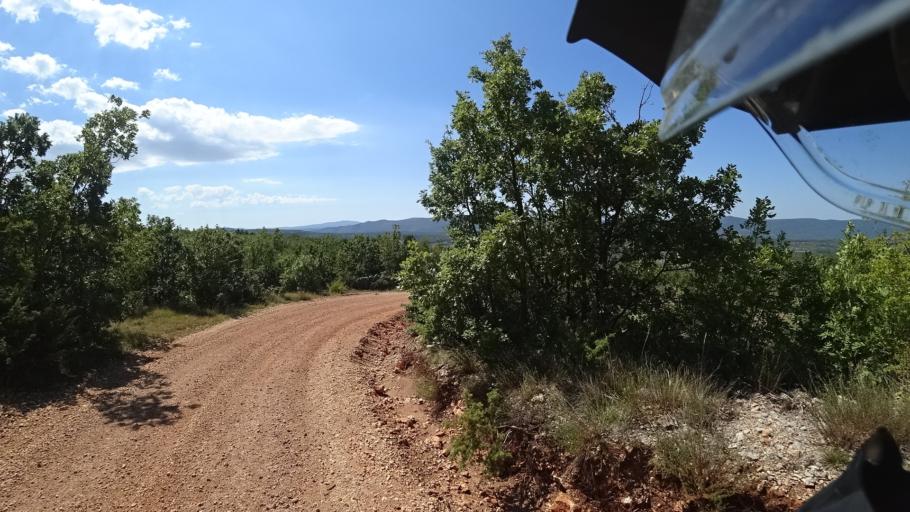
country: HR
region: Splitsko-Dalmatinska
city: Hrvace
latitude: 43.7550
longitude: 16.4569
